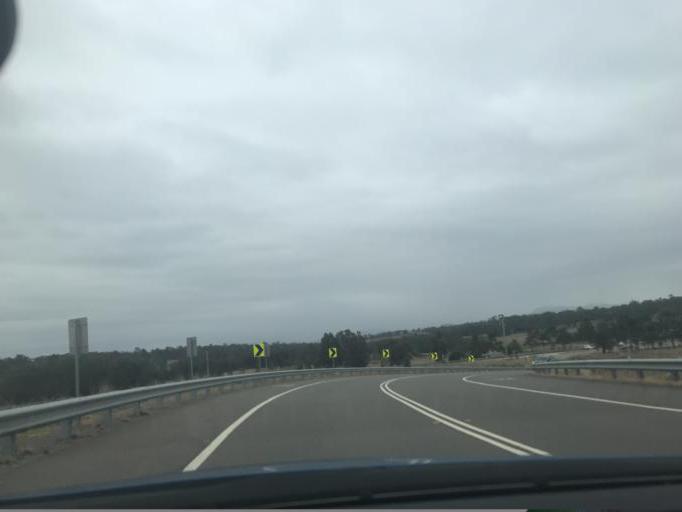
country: AU
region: New South Wales
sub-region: Cessnock
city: Branxton
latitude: -32.6556
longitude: 151.2738
